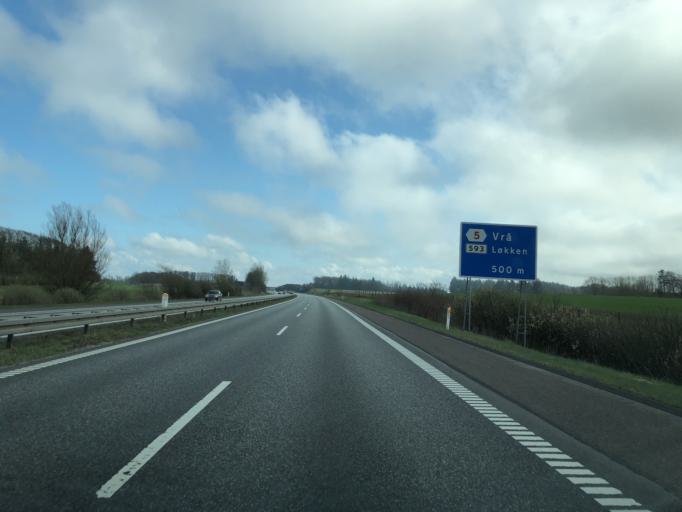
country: DK
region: North Denmark
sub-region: Hjorring Kommune
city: Vra
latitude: 57.3718
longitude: 10.0224
